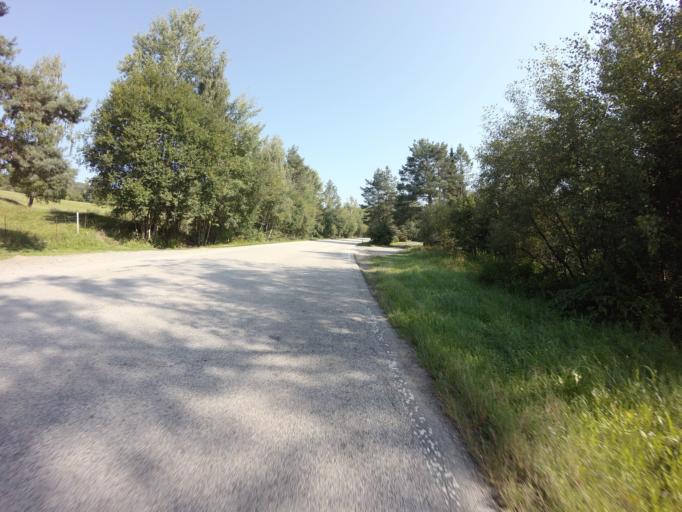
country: CZ
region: Jihocesky
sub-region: Okres Cesky Krumlov
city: Vyssi Brod
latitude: 48.5851
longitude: 14.3205
